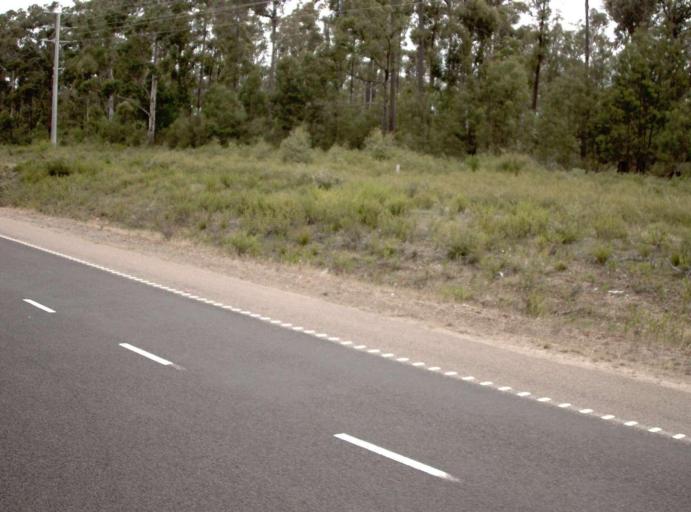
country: AU
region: Victoria
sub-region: East Gippsland
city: Lakes Entrance
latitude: -37.7177
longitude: 148.0772
